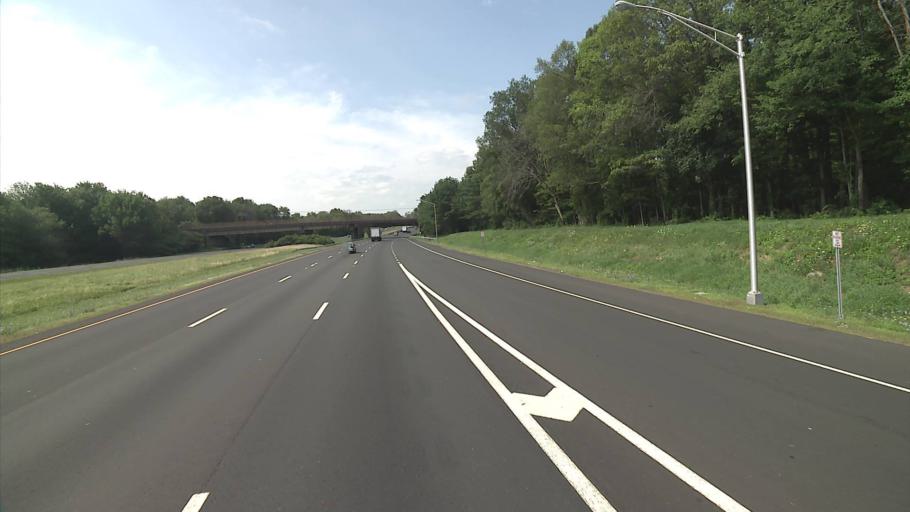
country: US
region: Connecticut
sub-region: New Haven County
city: Wallingford Center
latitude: 41.4563
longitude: -72.7800
